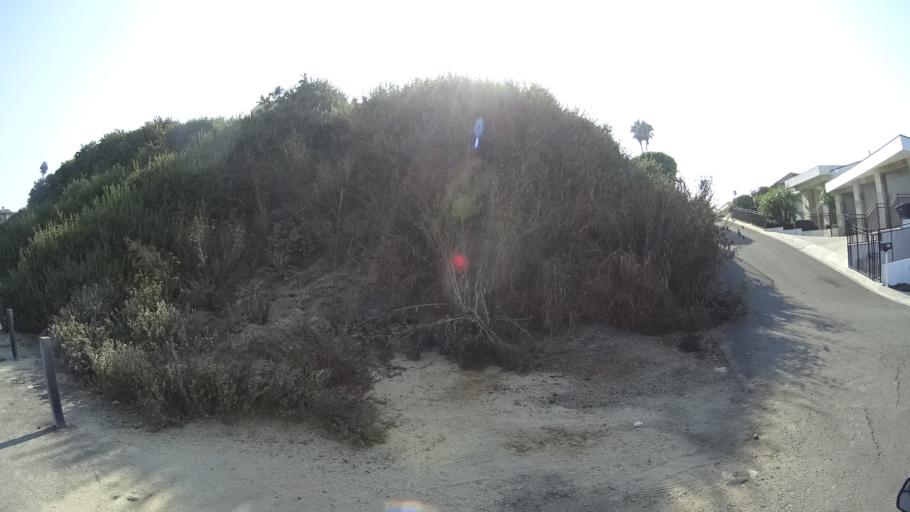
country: US
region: California
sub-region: Orange County
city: San Clemente
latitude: 33.4180
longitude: -117.6170
